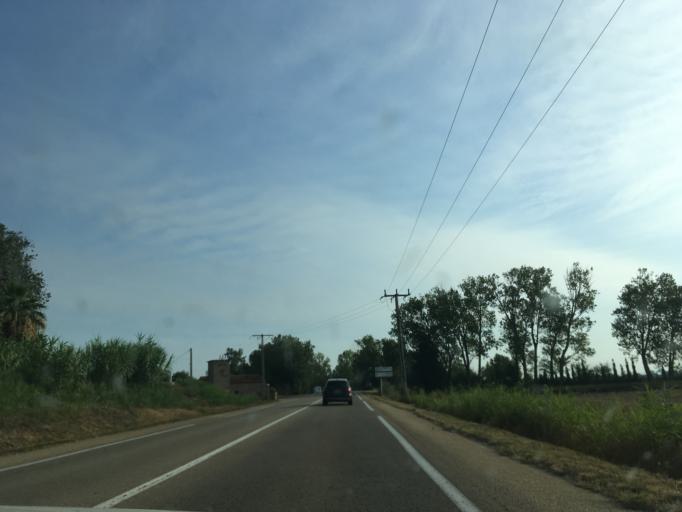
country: FR
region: Languedoc-Roussillon
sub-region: Departement du Gard
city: Saint-Gilles
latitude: 43.6066
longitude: 4.4765
